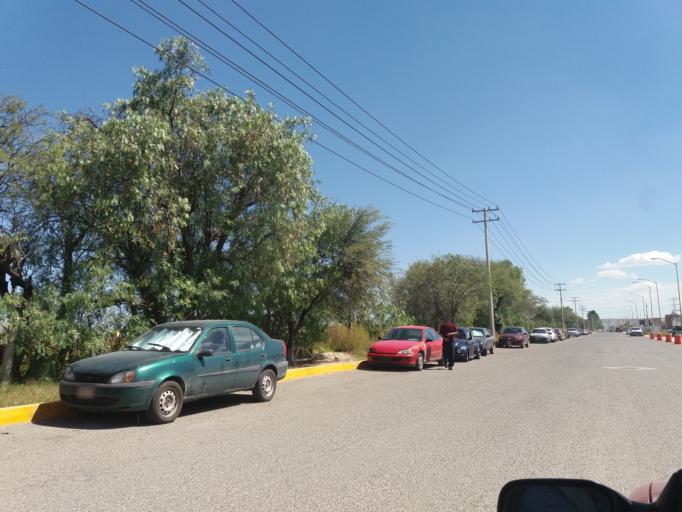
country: MX
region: Aguascalientes
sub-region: Aguascalientes
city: San Sebastian [Fraccionamiento]
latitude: 21.7999
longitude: -102.2968
